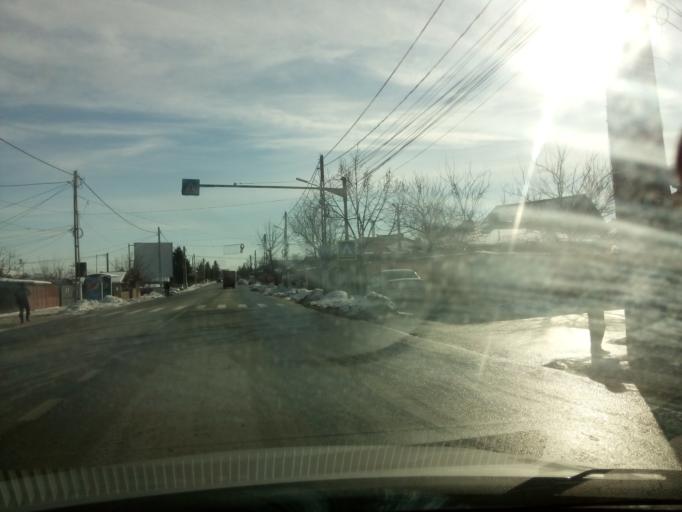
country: RO
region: Ilfov
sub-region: Comuna Popesti-Leordeni
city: Popesti-Leordeni
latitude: 44.3771
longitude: 26.1735
